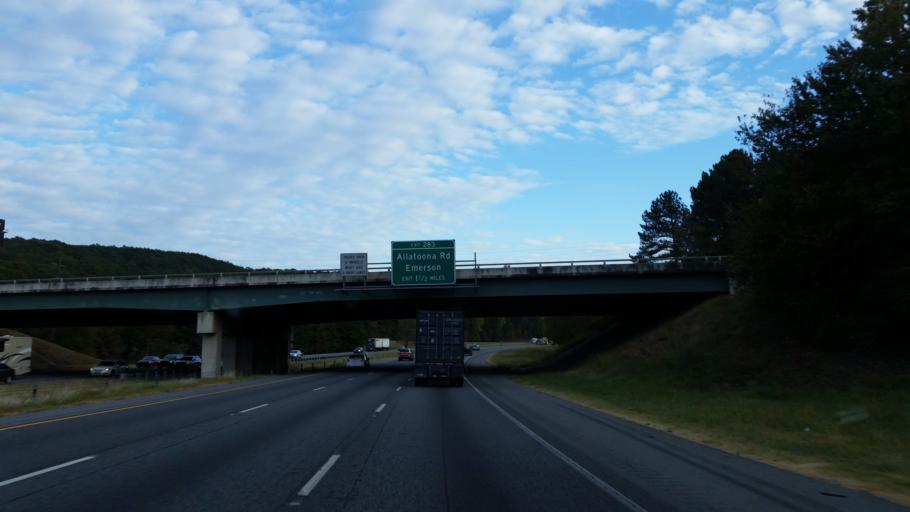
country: US
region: Georgia
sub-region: Bartow County
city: Emerson
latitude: 34.1431
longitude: -84.7396
